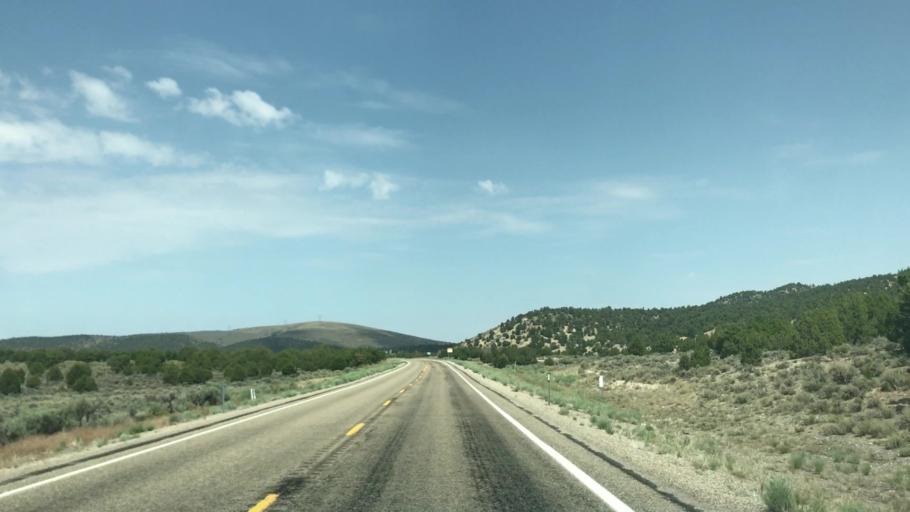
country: US
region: Nevada
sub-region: White Pine County
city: Ely
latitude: 39.3787
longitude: -115.0644
